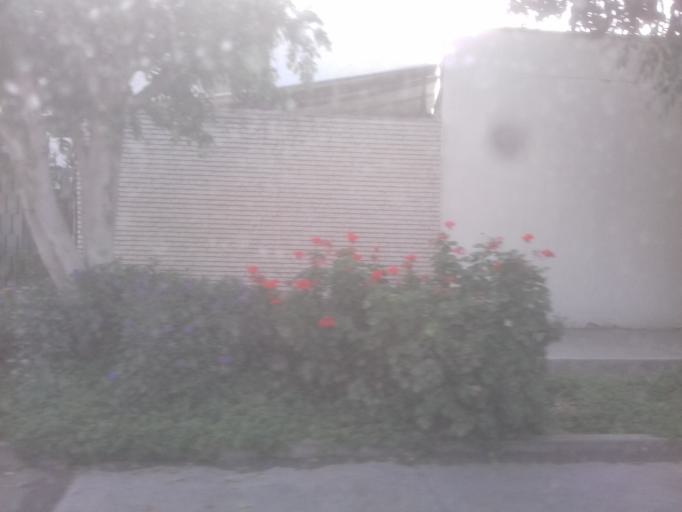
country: MX
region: Aguascalientes
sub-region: Aguascalientes
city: Aguascalientes
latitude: 21.8605
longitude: -102.2909
